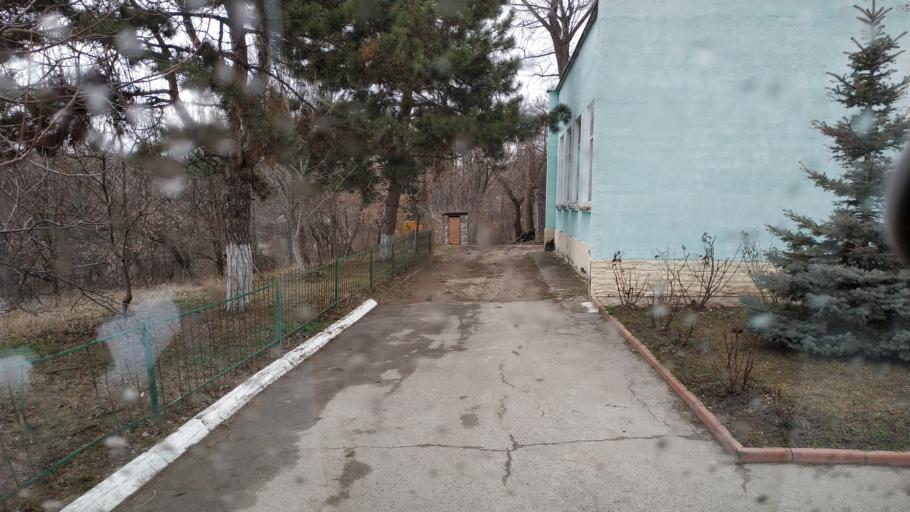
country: MD
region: Calarasi
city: Calarasi
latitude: 47.2694
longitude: 28.3462
